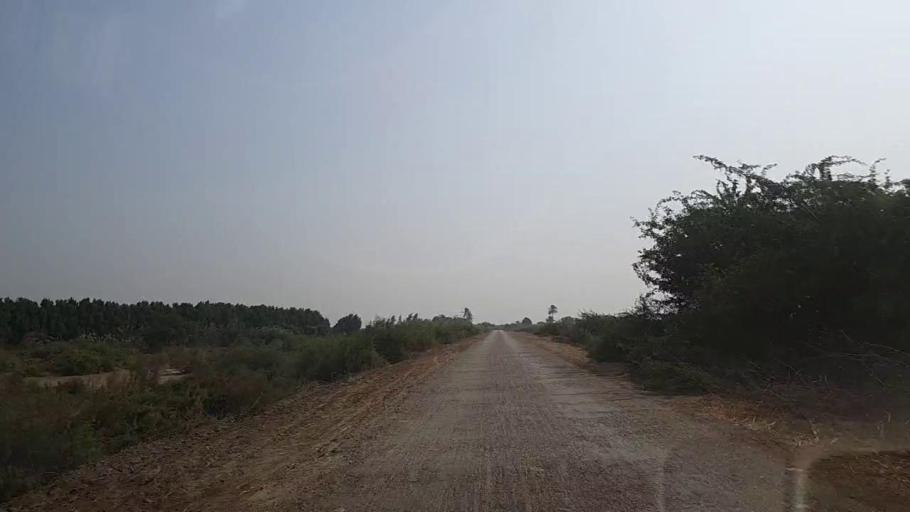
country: PK
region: Sindh
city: Keti Bandar
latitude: 24.2384
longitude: 67.6393
